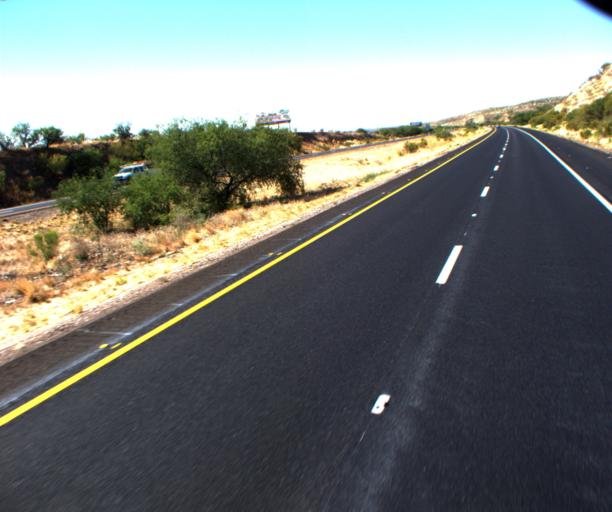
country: US
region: Arizona
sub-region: Santa Cruz County
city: Tubac
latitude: 31.5891
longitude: -111.0543
